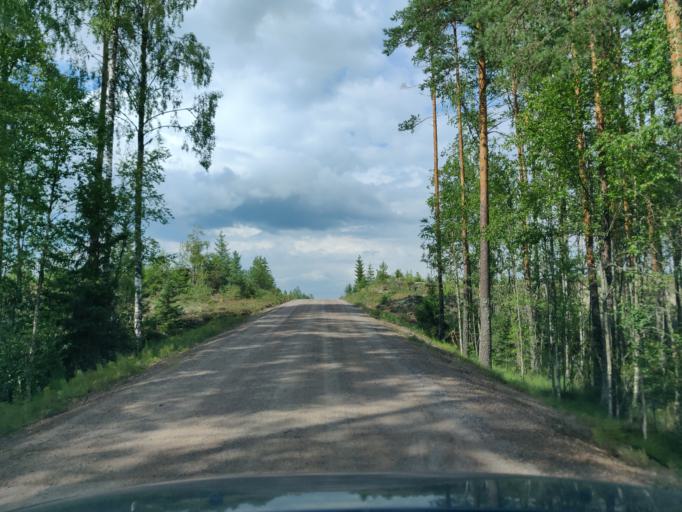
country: SE
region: Vaermland
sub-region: Hagfors Kommun
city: Hagfors
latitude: 59.9746
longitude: 13.5484
